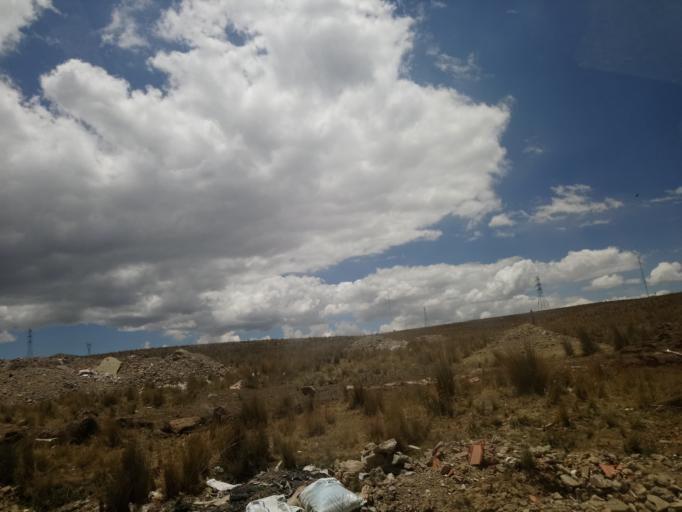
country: BO
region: La Paz
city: La Paz
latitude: -16.4384
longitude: -68.1631
